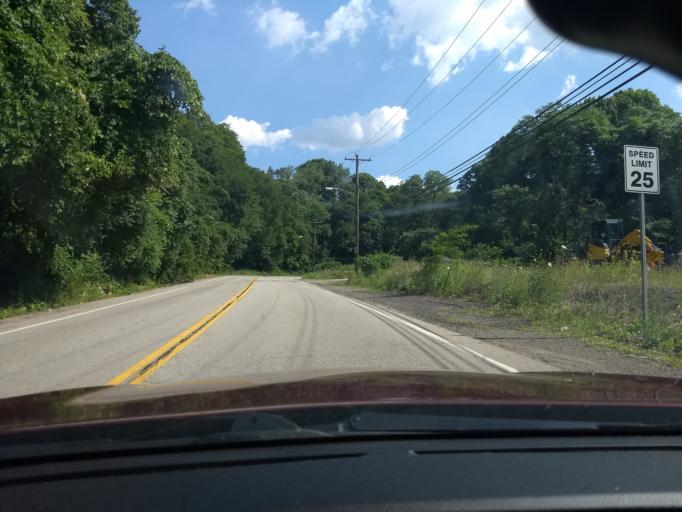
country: US
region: Pennsylvania
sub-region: Allegheny County
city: Munhall
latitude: 40.3924
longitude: -79.9031
